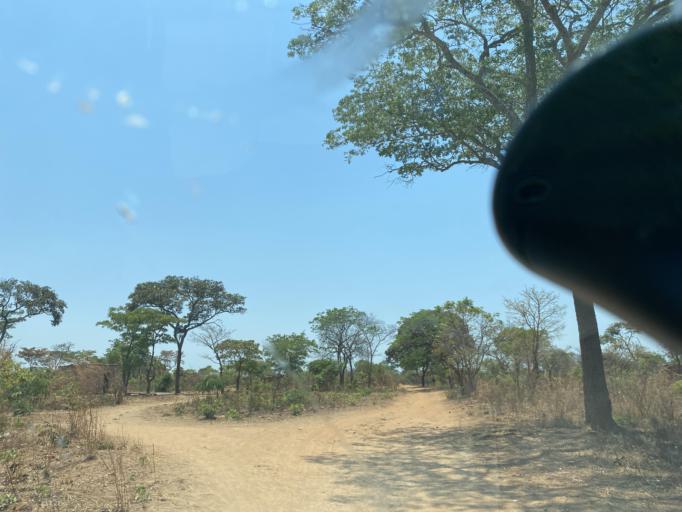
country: ZM
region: Lusaka
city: Chongwe
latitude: -15.4421
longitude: 29.2236
